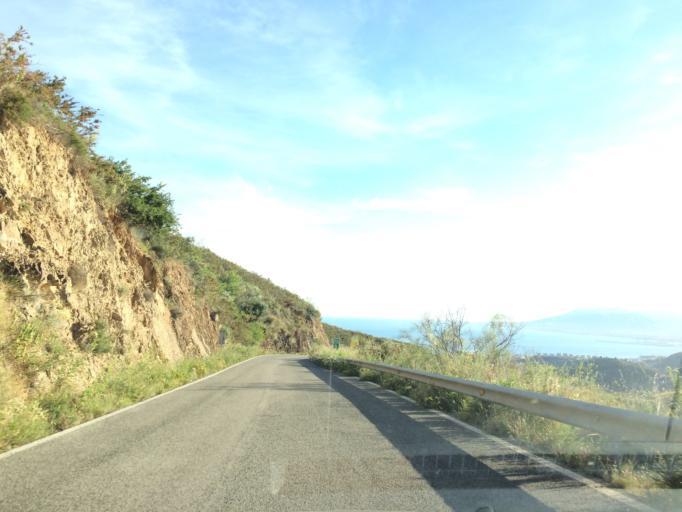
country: ES
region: Andalusia
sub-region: Provincia de Malaga
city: Totalan
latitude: 36.7437
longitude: -4.3295
